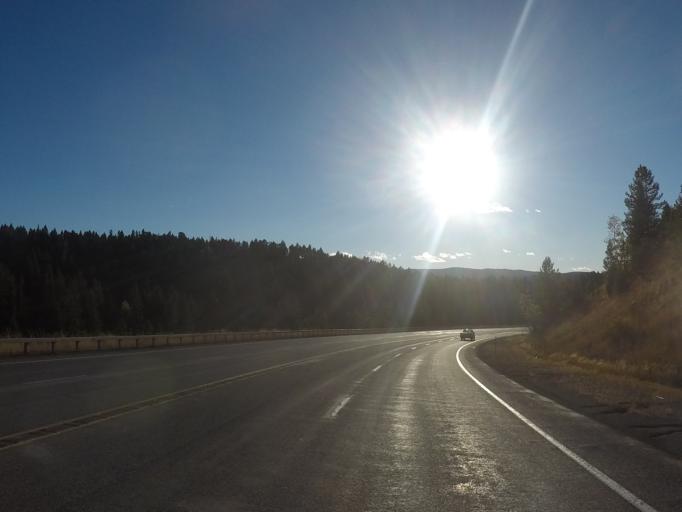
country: US
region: Montana
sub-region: Lewis and Clark County
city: Helena West Side
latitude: 46.5568
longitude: -112.3611
